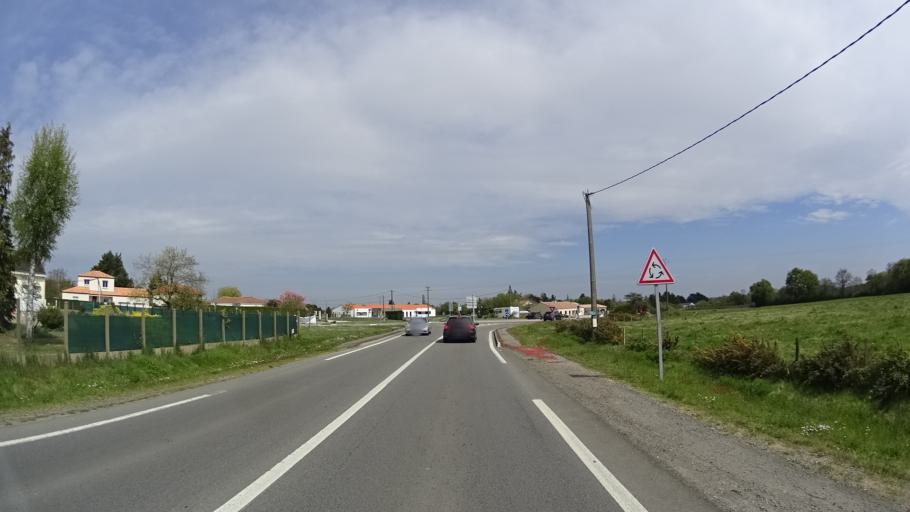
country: FR
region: Pays de la Loire
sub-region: Departement de la Loire-Atlantique
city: Port-Saint-Pere
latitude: 47.1294
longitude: -1.7590
